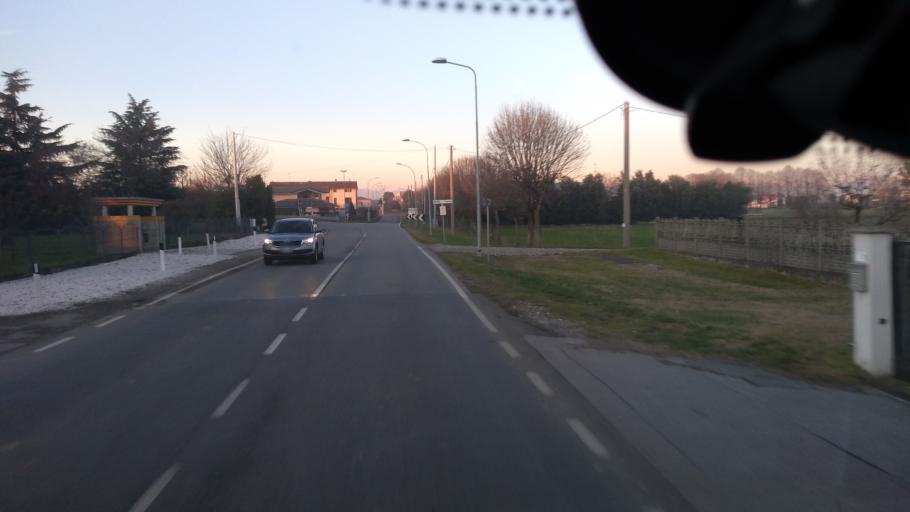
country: IT
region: Lombardy
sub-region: Provincia di Bergamo
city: Calvenzano
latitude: 45.4880
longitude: 9.6009
